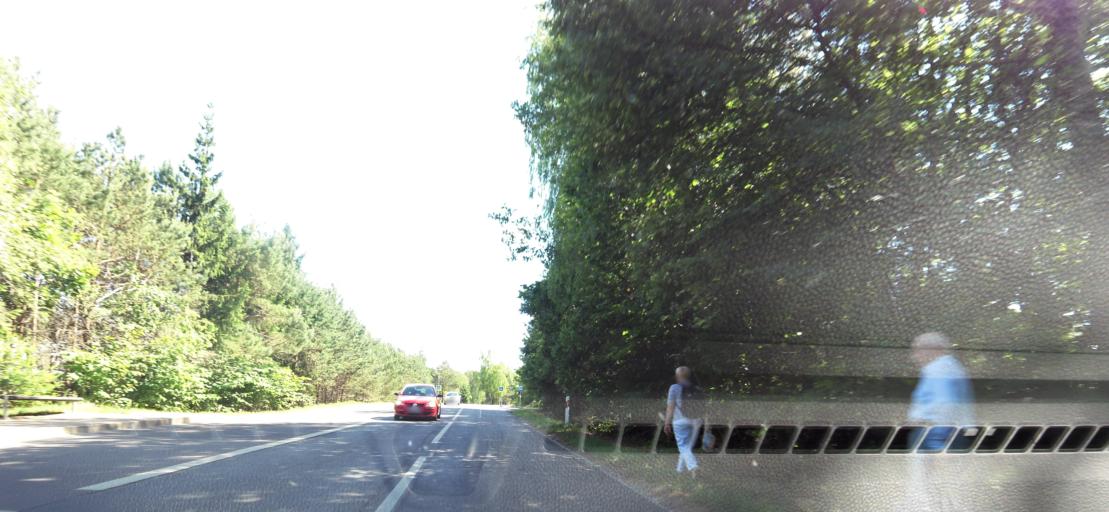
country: LT
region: Vilnius County
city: Rasos
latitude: 54.7923
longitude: 25.3510
